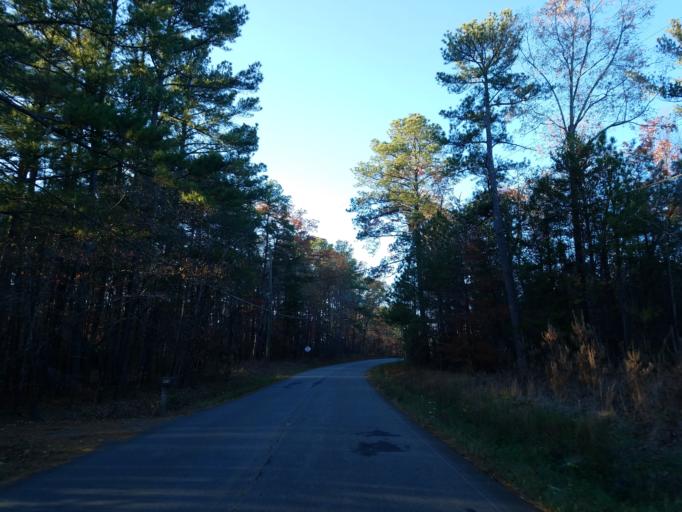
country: US
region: Georgia
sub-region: Pickens County
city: Nelson
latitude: 34.3632
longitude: -84.3714
